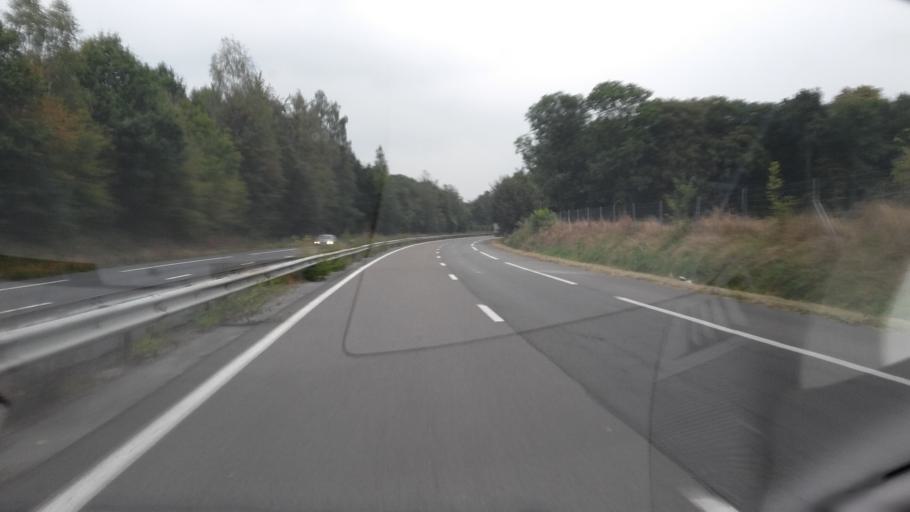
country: FR
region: Champagne-Ardenne
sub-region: Departement des Ardennes
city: Bazeilles
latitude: 49.7108
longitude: 5.0114
